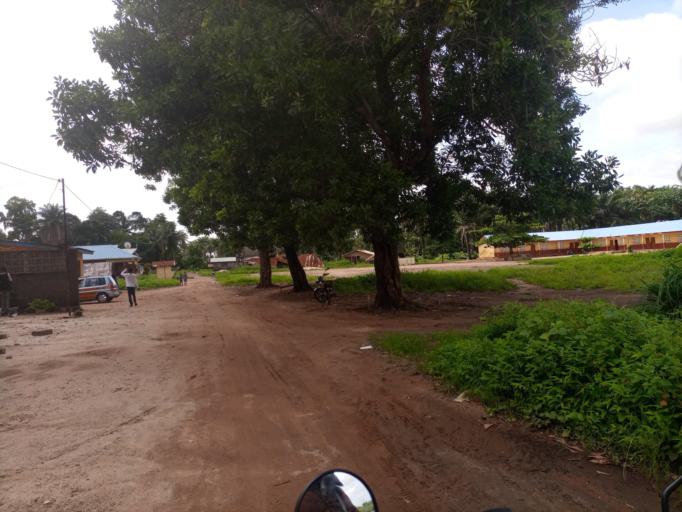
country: SL
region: Northern Province
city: Masoyila
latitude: 8.6195
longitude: -13.1739
